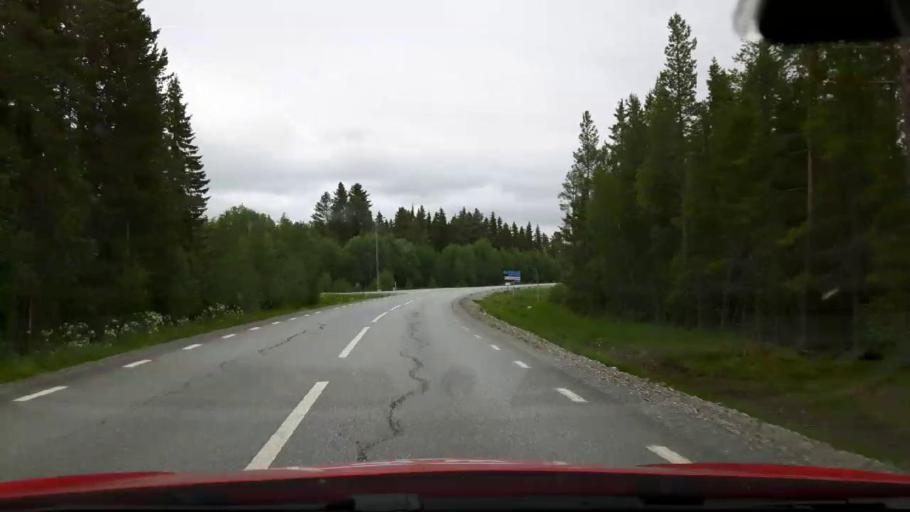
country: SE
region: Jaemtland
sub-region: OEstersunds Kommun
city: Lit
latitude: 63.7351
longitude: 14.7418
